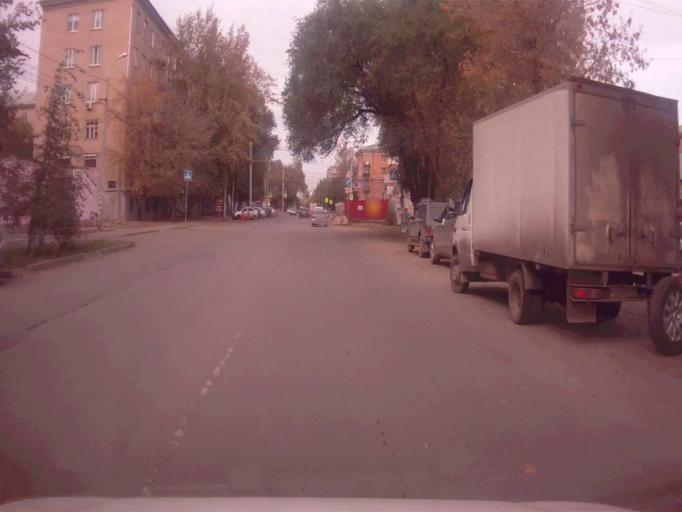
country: RU
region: Chelyabinsk
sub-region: Gorod Chelyabinsk
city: Chelyabinsk
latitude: 55.1593
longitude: 61.4217
